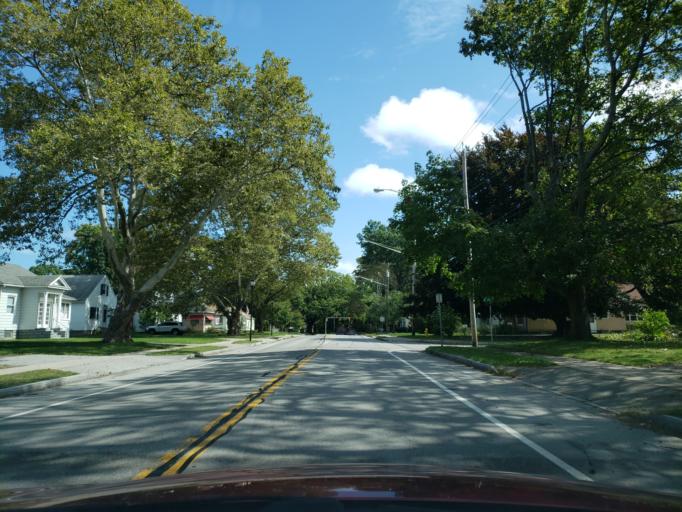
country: US
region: New York
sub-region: Monroe County
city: Greece
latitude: 43.2311
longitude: -77.6494
